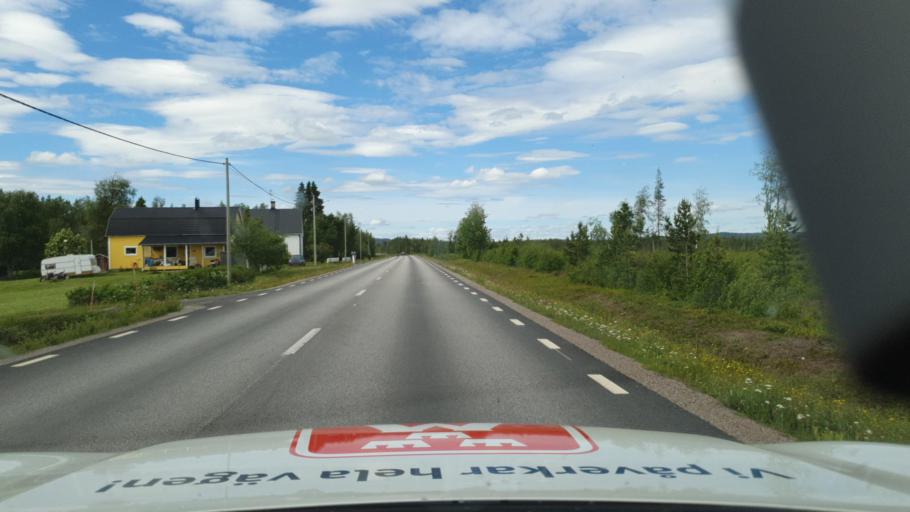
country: SE
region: Vaesterbotten
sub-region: Norsjo Kommun
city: Norsjoe
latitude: 65.2279
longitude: 19.7446
